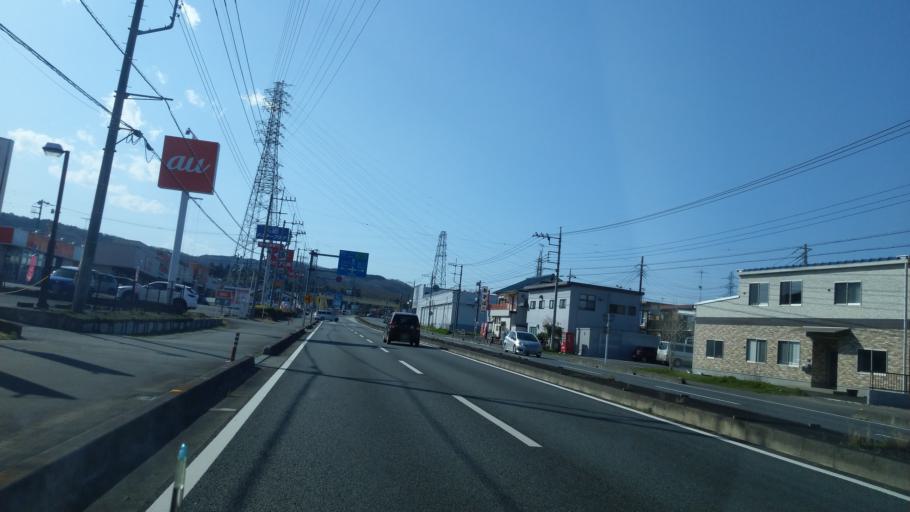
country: JP
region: Saitama
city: Ogawa
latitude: 36.0387
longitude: 139.3212
